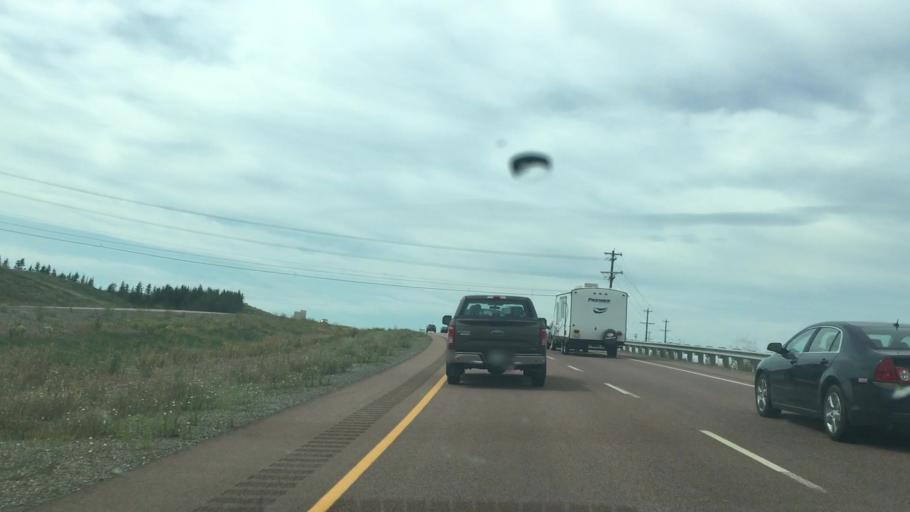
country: CA
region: Nova Scotia
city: Antigonish
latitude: 45.6041
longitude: -61.9268
